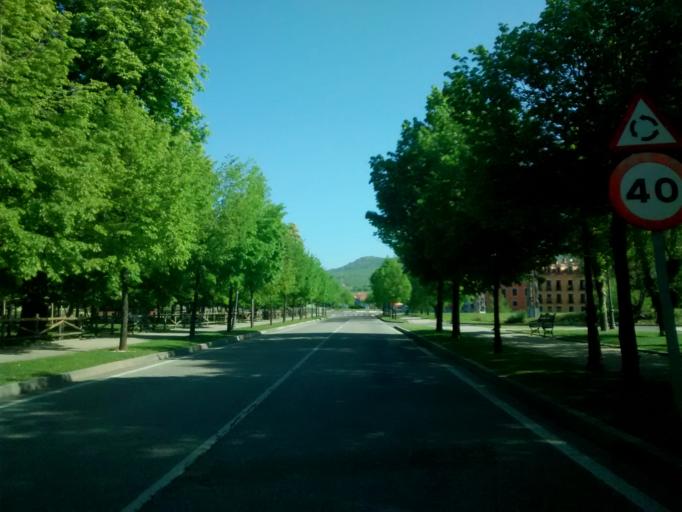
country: ES
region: Castille and Leon
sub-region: Provincia de Segovia
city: San Ildefonso
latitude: 40.9043
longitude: -4.0088
